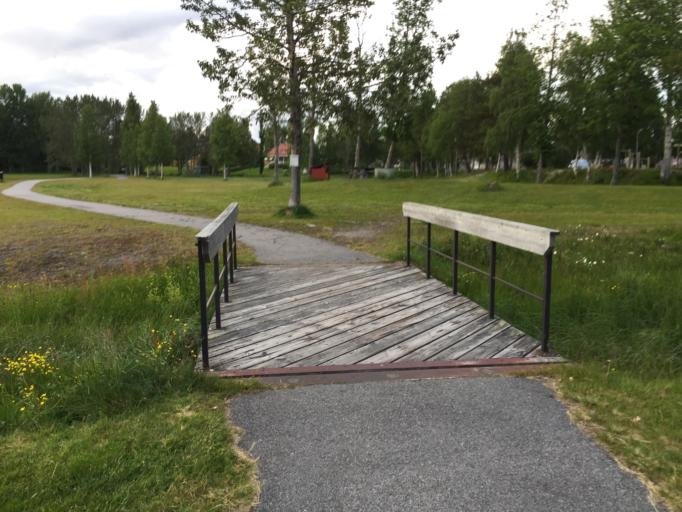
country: SE
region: Vaesterbotten
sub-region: Storumans Kommun
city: Storuman
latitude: 65.1015
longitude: 17.1194
